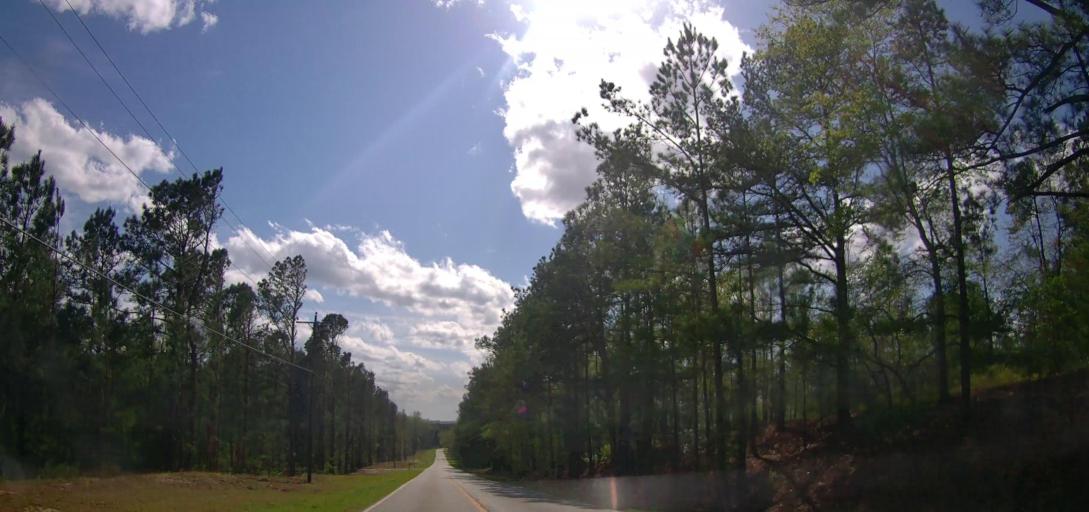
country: US
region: Georgia
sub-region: Wilkinson County
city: Gordon
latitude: 32.8097
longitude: -83.4089
